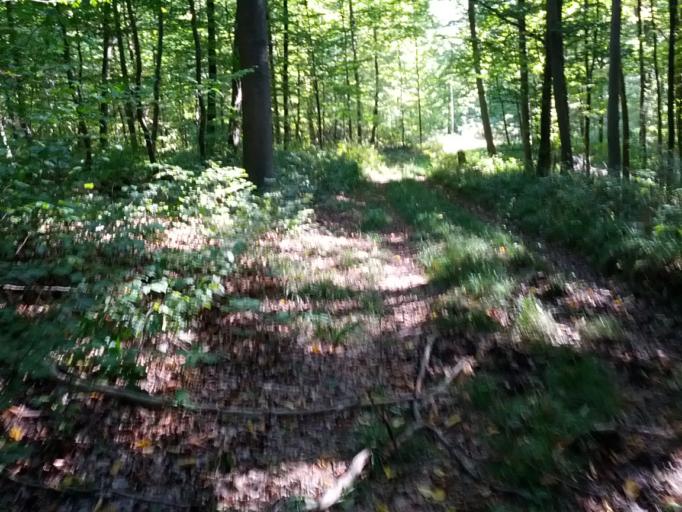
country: DE
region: Thuringia
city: Eisenach
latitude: 50.9983
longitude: 10.2929
